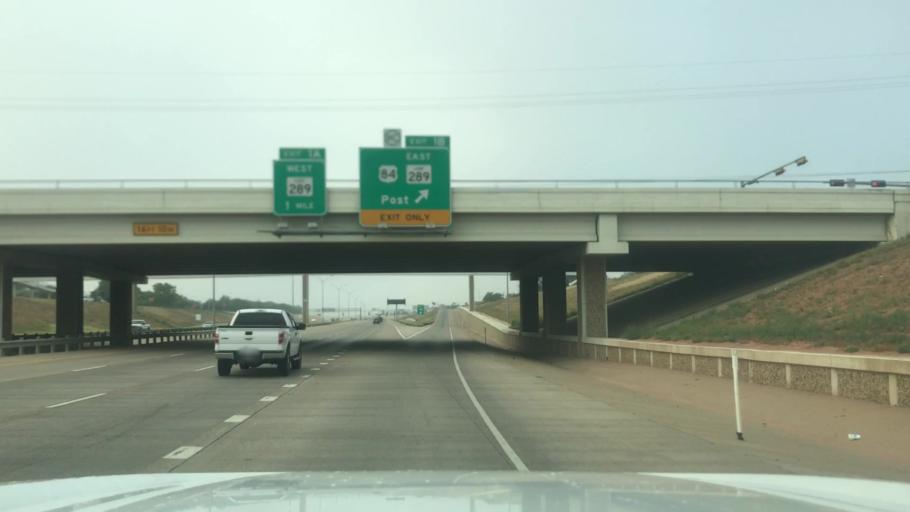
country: US
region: Texas
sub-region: Lubbock County
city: Lubbock
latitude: 33.5494
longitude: -101.8453
